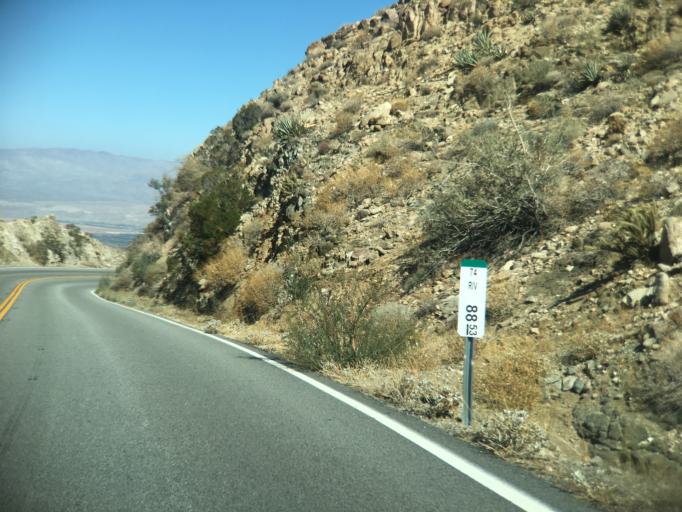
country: US
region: California
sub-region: Riverside County
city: Palm Desert
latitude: 33.6508
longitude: -116.4028
